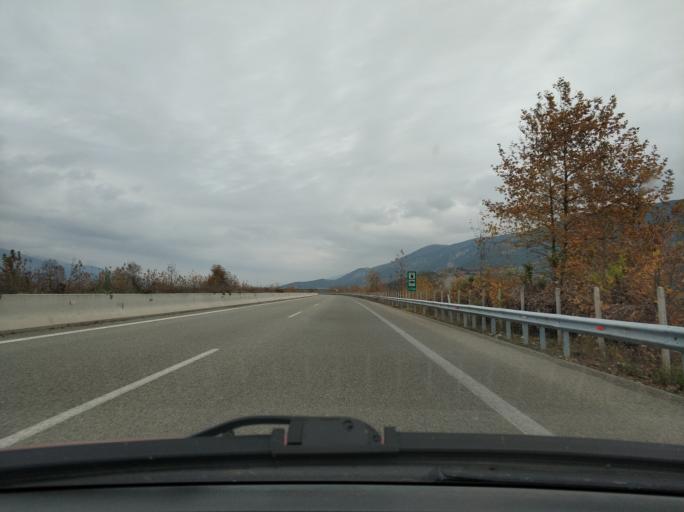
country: GR
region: East Macedonia and Thrace
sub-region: Nomos Kavalas
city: Nikisiani
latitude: 40.8261
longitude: 24.0898
